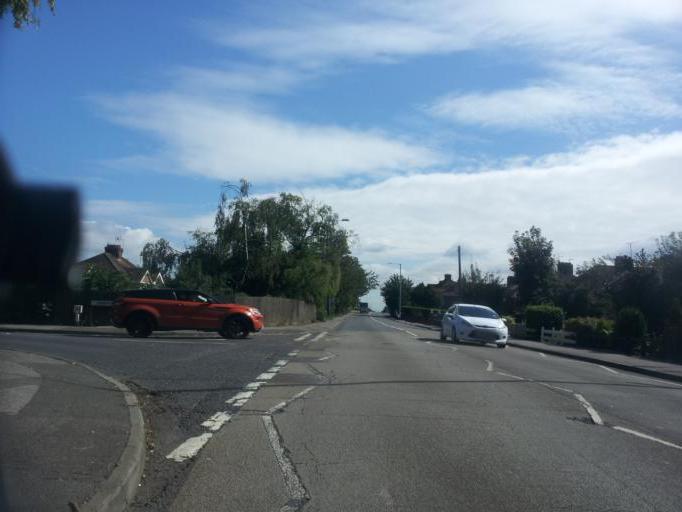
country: GB
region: England
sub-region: Kent
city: Sittingbourne
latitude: 51.3448
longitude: 0.7077
